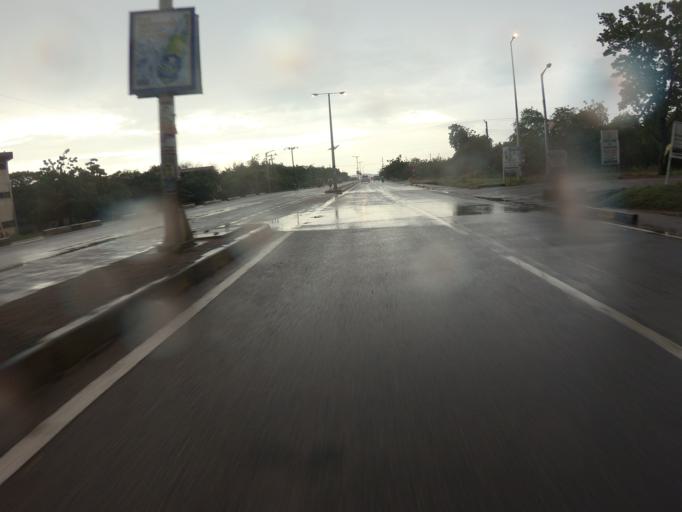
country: GH
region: Upper East
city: Bolgatanga
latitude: 10.7988
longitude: -0.8599
